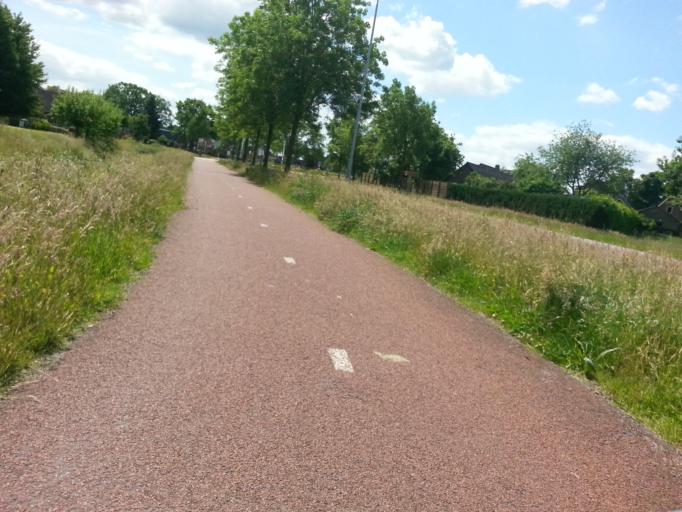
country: NL
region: Gelderland
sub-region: Gemeente Barneveld
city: Barneveld
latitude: 52.1345
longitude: 5.6035
